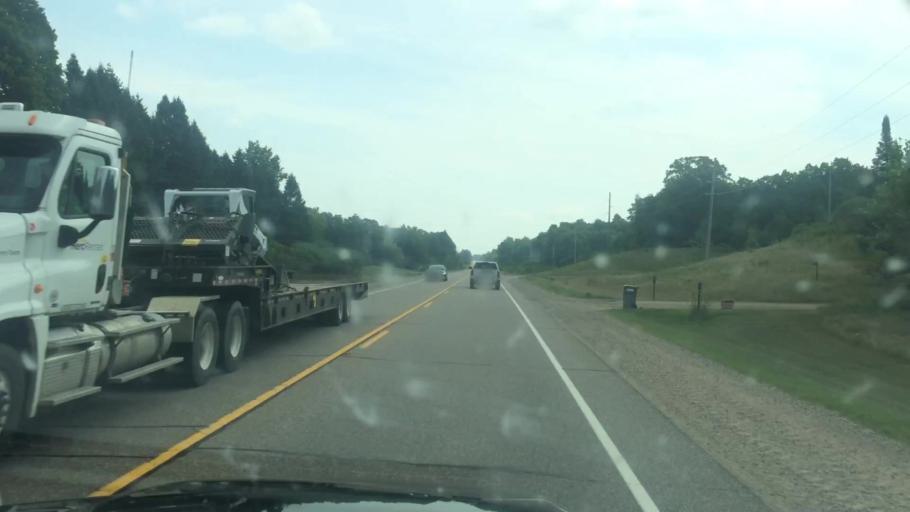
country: US
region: Wisconsin
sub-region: Langlade County
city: Antigo
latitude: 45.1616
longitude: -89.0543
